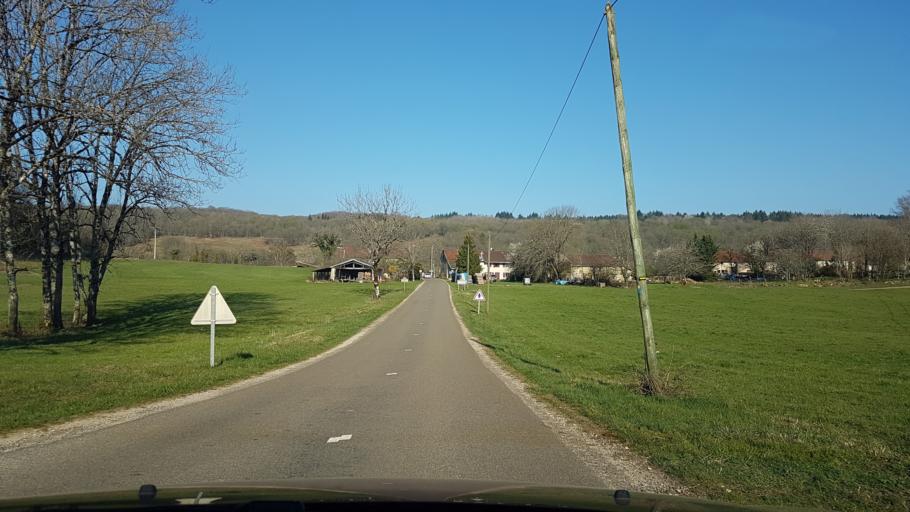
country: FR
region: Franche-Comte
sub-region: Departement du Jura
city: Orgelet
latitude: 46.5059
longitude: 5.5256
